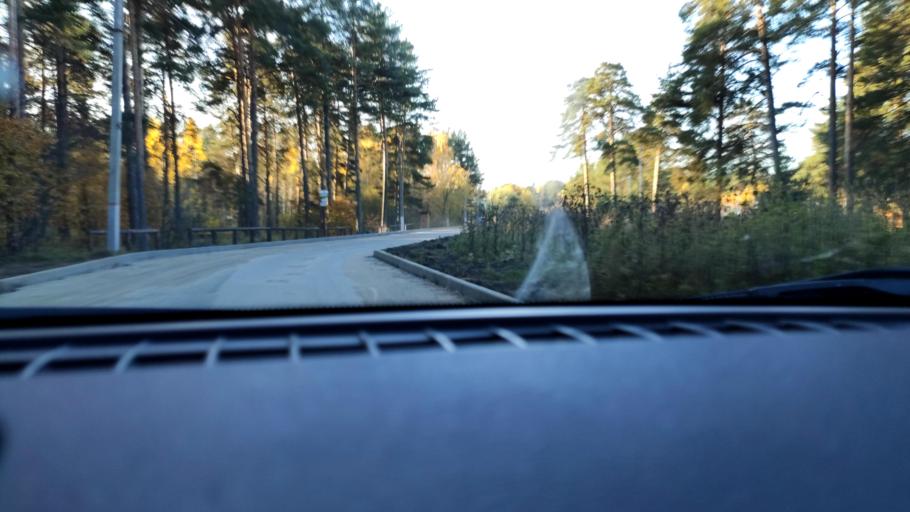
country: RU
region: Perm
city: Kondratovo
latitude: 57.9918
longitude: 56.1431
